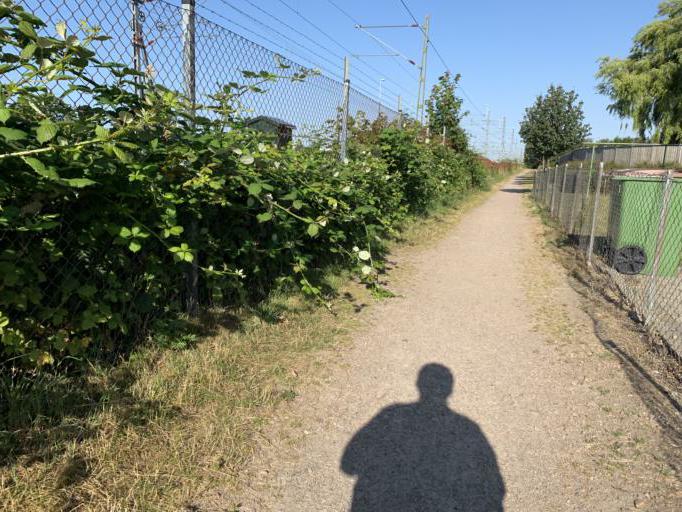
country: SE
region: Skane
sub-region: Trelleborgs Kommun
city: Trelleborg
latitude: 55.3679
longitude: 13.1818
